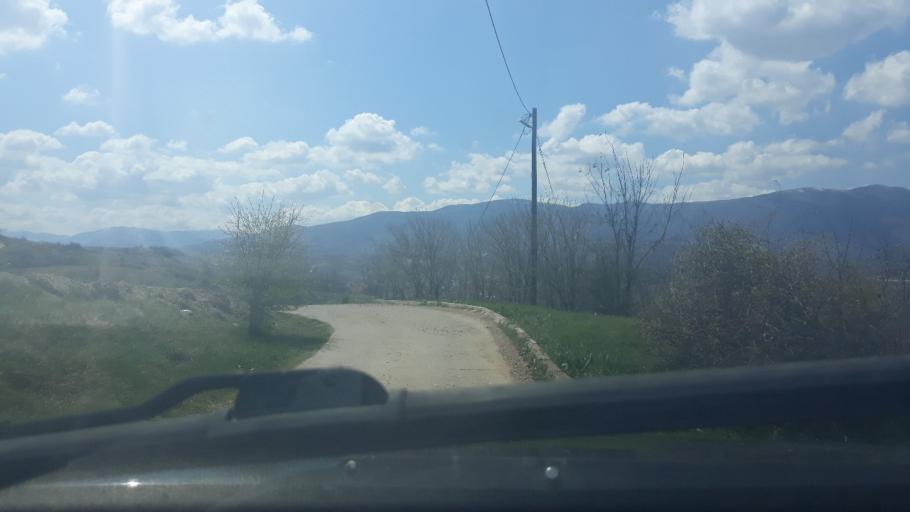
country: MK
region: Caska
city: Caska
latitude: 41.6472
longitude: 21.6942
